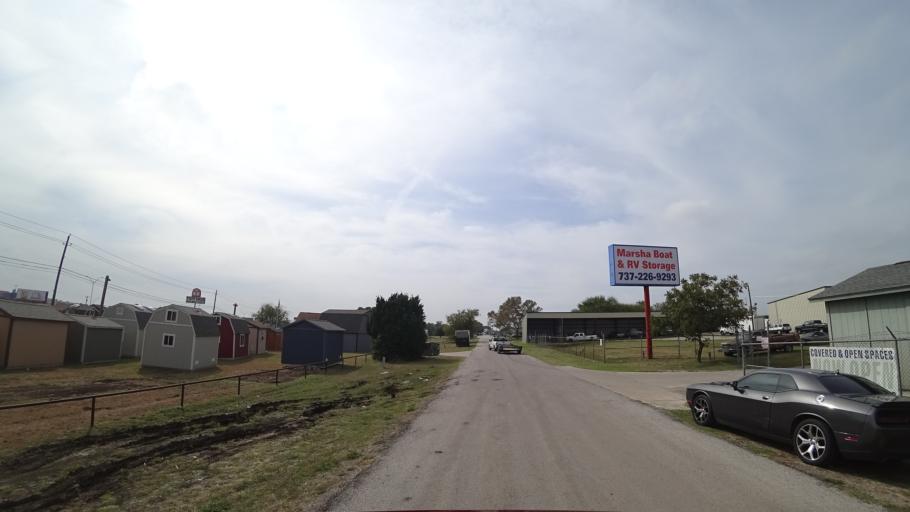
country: US
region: Texas
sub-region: Travis County
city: Wells Branch
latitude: 30.4521
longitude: -97.6671
